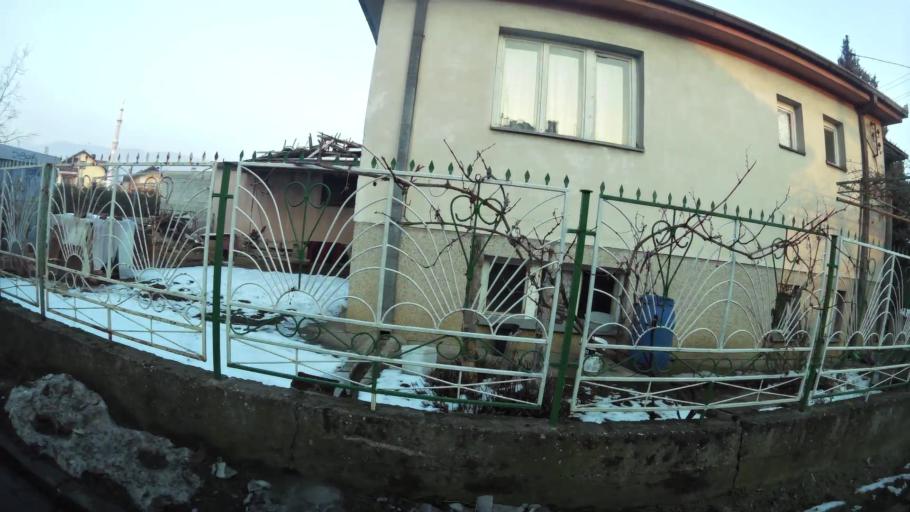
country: MK
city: Creshevo
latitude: 42.0133
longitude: 21.5132
